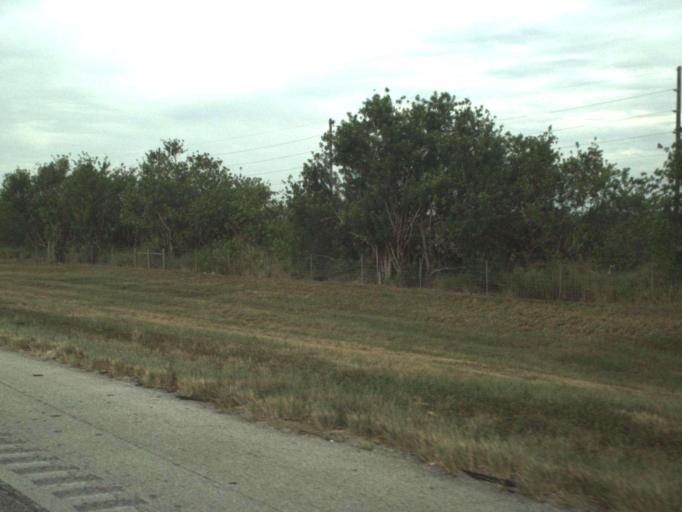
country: US
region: Florida
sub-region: Saint Lucie County
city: Port Saint Lucie
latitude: 27.2024
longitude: -80.4008
